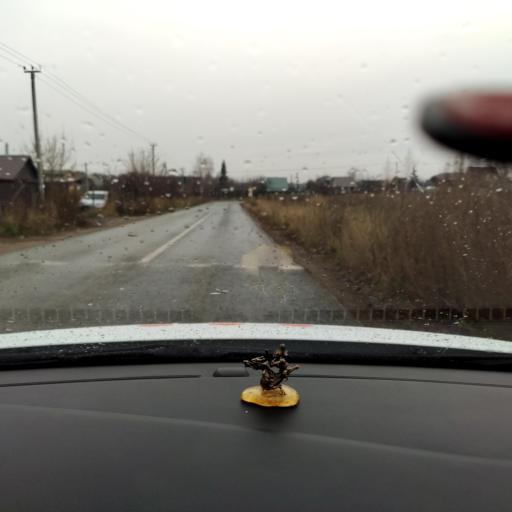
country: RU
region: Tatarstan
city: Vysokaya Gora
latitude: 55.8301
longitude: 49.2293
